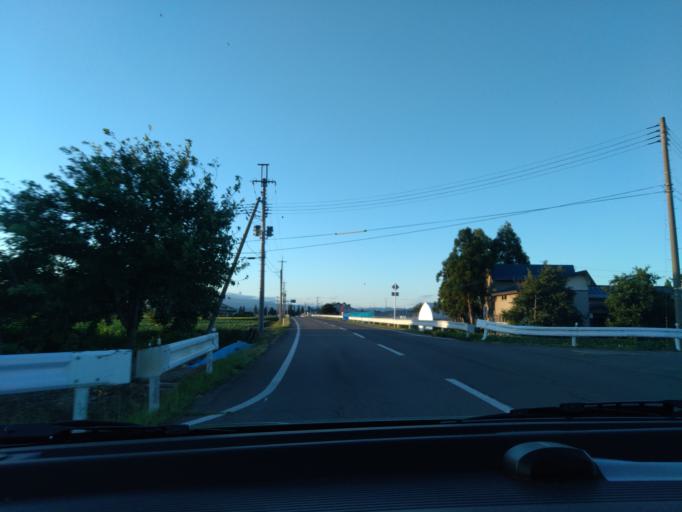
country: JP
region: Akita
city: Kakunodatemachi
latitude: 39.5024
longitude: 140.5598
